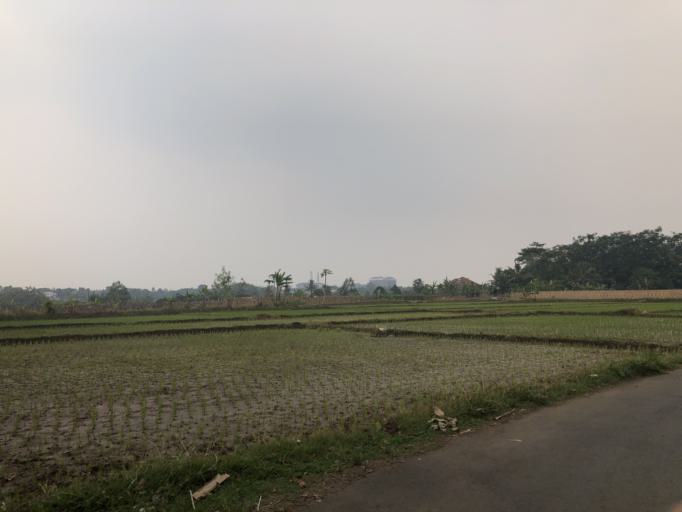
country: ID
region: West Java
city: Ciampea
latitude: -6.5651
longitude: 106.7456
